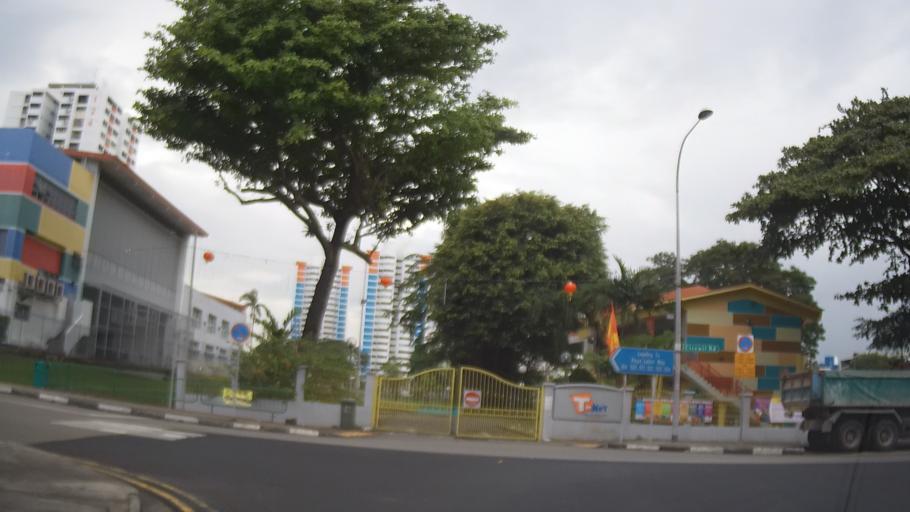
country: SG
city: Singapore
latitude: 1.3239
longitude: 103.8852
